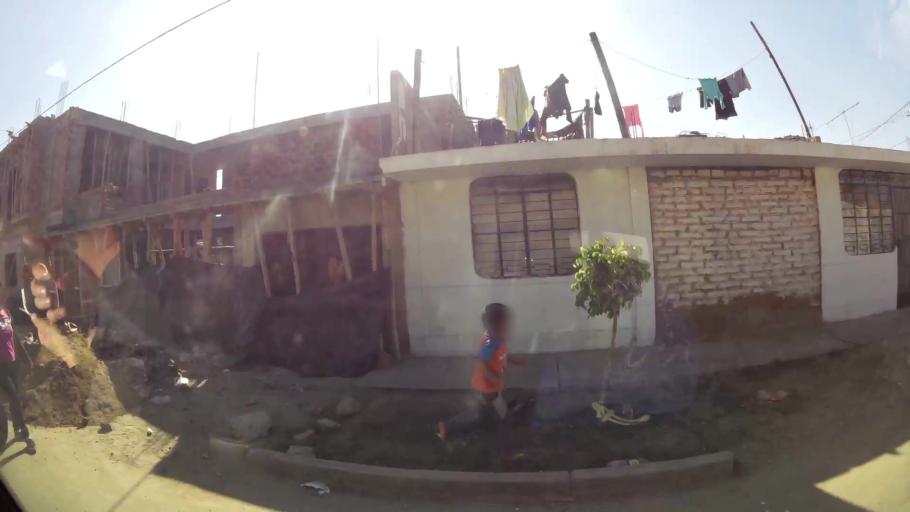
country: PE
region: Ica
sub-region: Provincia de Ica
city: La Tinguina
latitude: -14.0442
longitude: -75.7102
